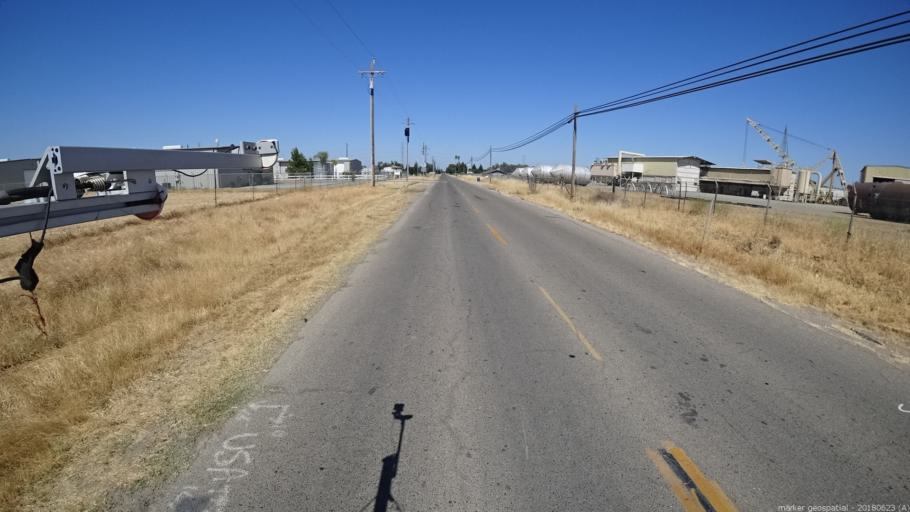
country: US
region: California
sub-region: Madera County
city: Parksdale
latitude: 36.9744
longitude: -120.0204
